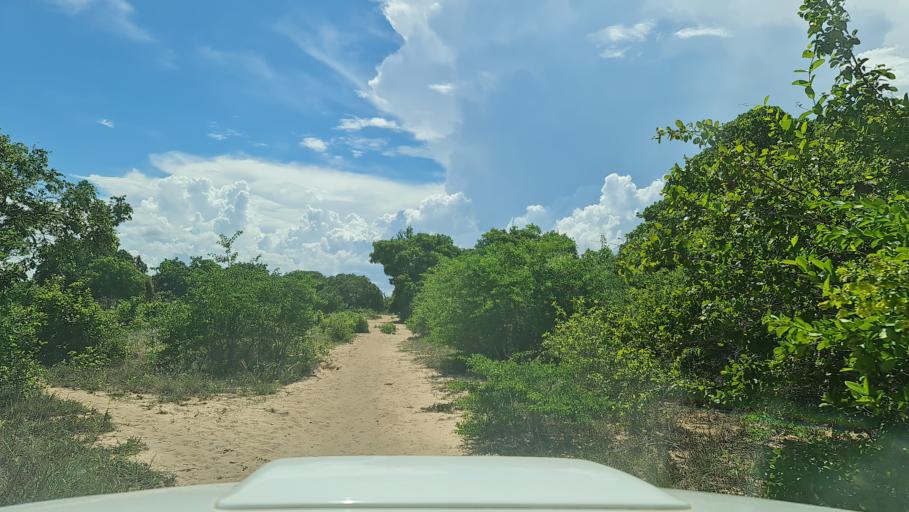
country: MZ
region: Nampula
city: Antonio Enes
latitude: -15.7066
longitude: 40.2588
